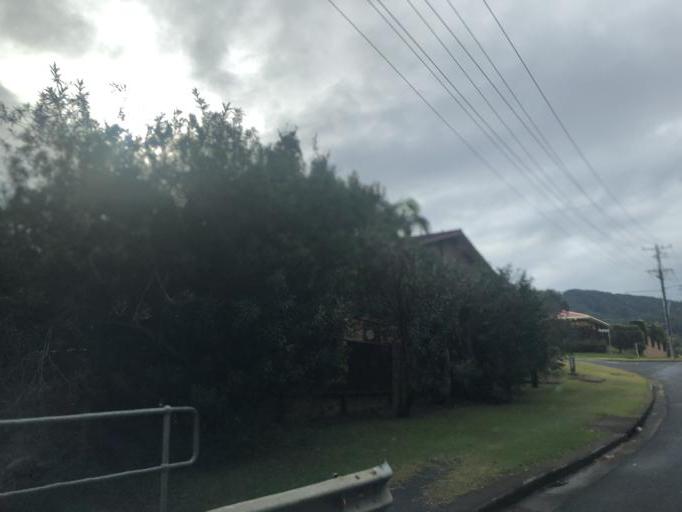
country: AU
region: New South Wales
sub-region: Coffs Harbour
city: Coffs Harbour
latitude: -30.2861
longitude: 153.1110
